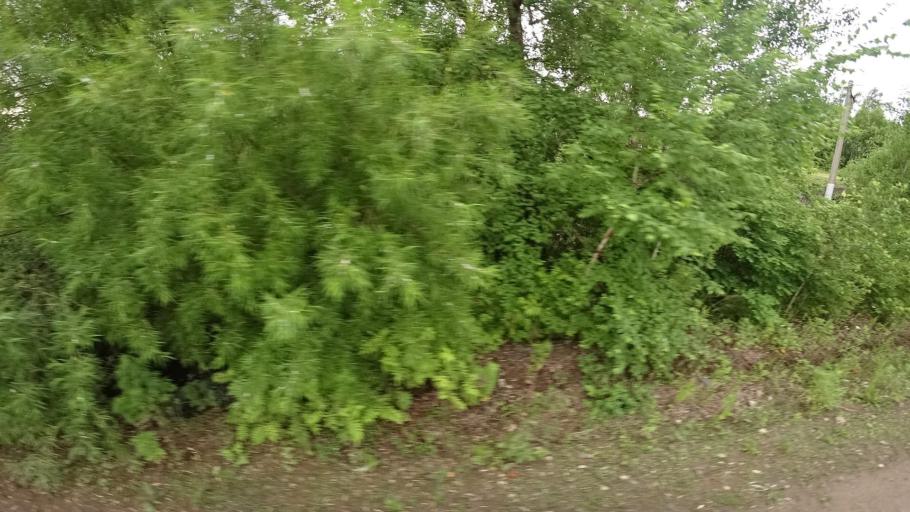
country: RU
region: Khabarovsk Krai
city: Amursk
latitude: 49.9158
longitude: 136.1619
